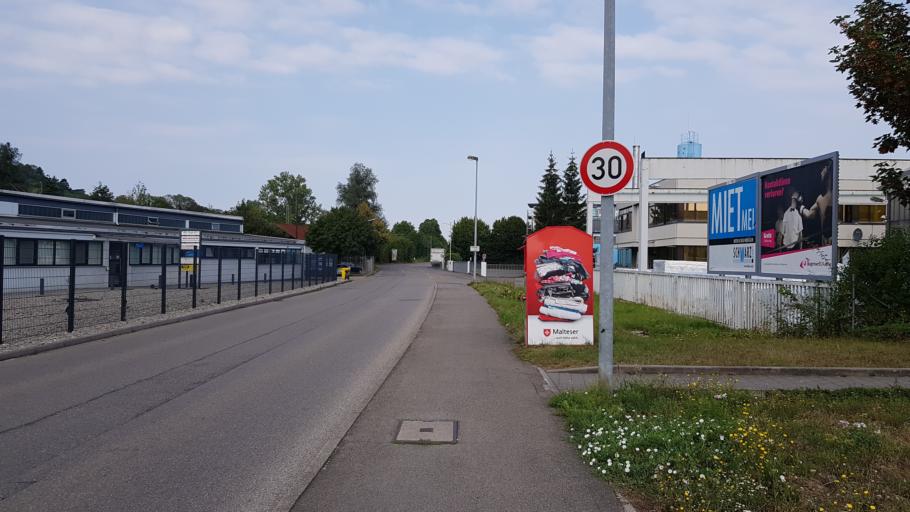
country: DE
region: Baden-Wuerttemberg
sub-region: Regierungsbezirk Stuttgart
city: Winterbach
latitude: 48.8087
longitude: 9.4308
